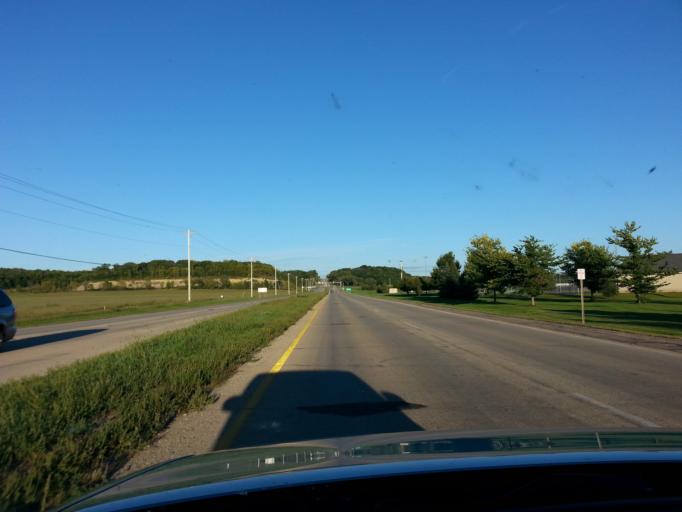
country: US
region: Minnesota
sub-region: Olmsted County
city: Rochester
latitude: 44.0215
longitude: -92.4283
